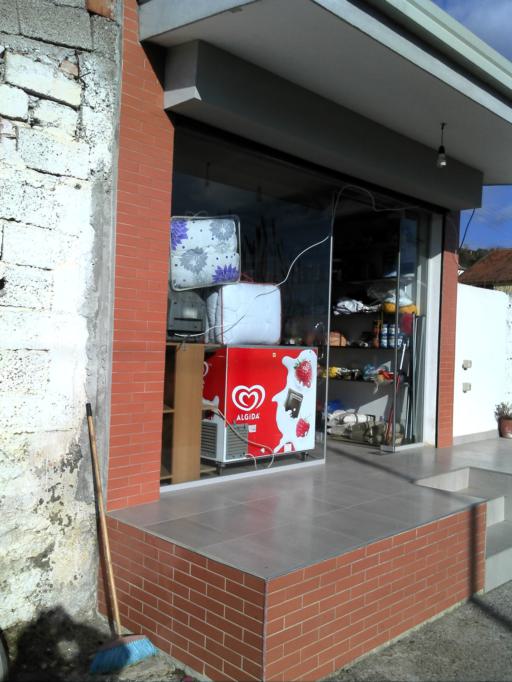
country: AL
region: Shkoder
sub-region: Rrethi i Shkodres
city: Dajc
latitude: 42.0121
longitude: 19.4097
